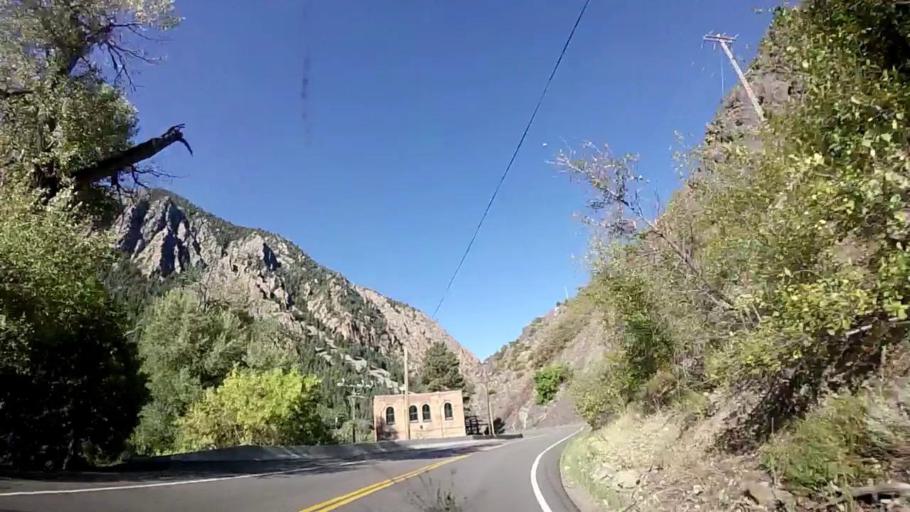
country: US
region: Utah
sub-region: Salt Lake County
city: Cottonwood Heights
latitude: 40.6238
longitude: -111.7527
